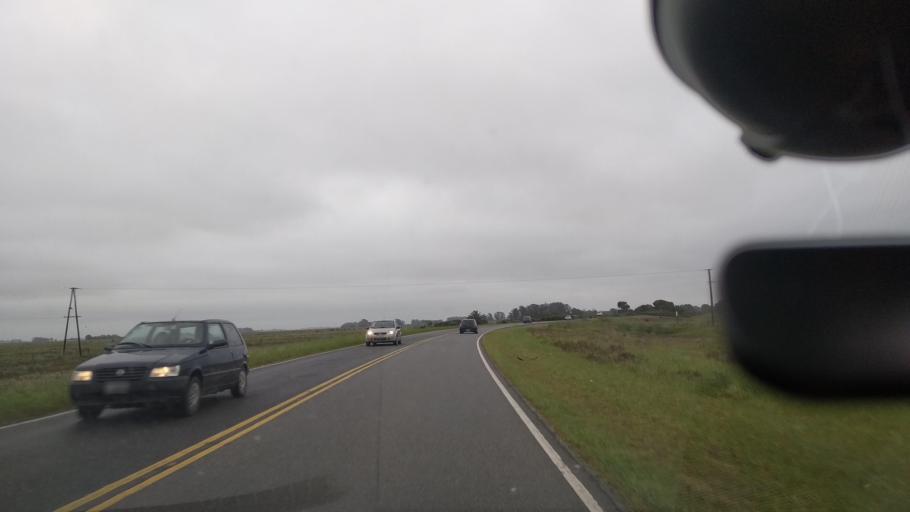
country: AR
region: Buenos Aires
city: Veronica
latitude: -35.4419
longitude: -57.3420
